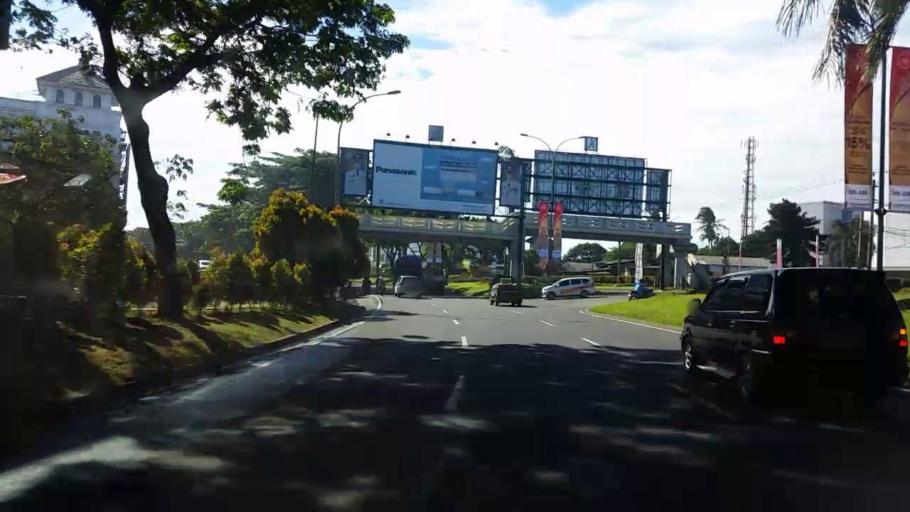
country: ID
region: West Java
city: Serpong
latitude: -6.3039
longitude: 106.6689
